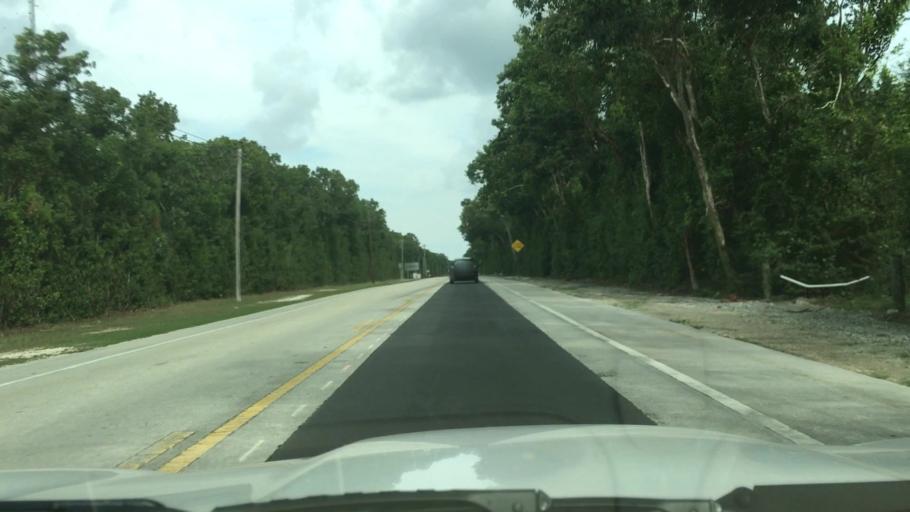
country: US
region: Florida
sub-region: Monroe County
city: North Key Largo
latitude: 25.2342
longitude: -80.3255
